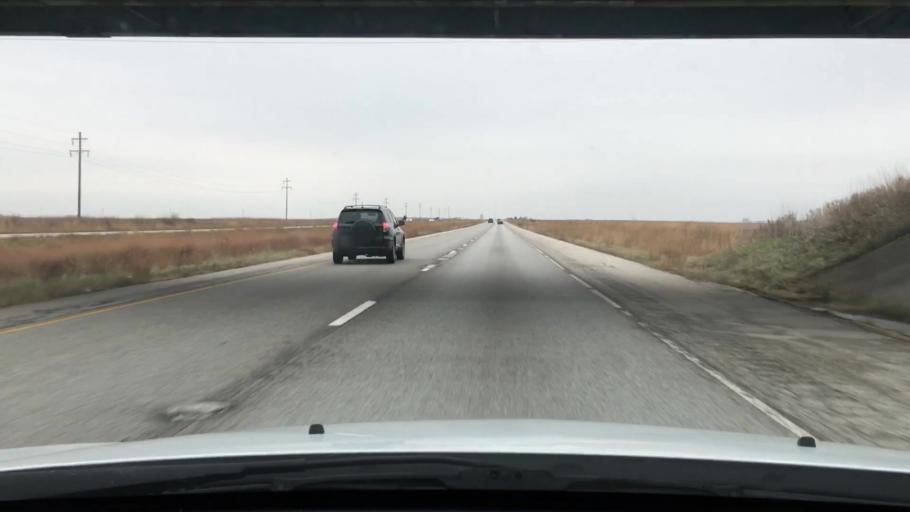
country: US
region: Illinois
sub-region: Morgan County
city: Jacksonville
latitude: 39.7379
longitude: -90.1264
